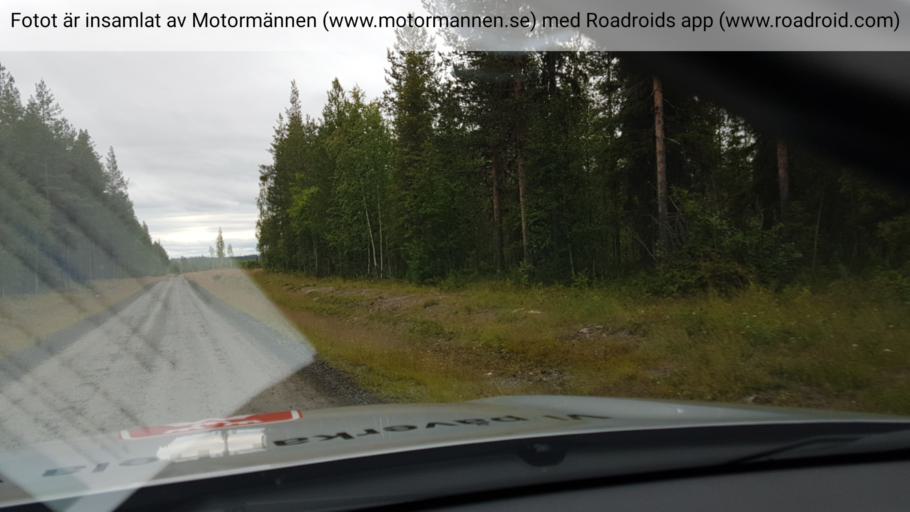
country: SE
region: Norrbotten
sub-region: Pajala Kommun
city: Pajala
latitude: 67.0107
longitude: 22.8523
